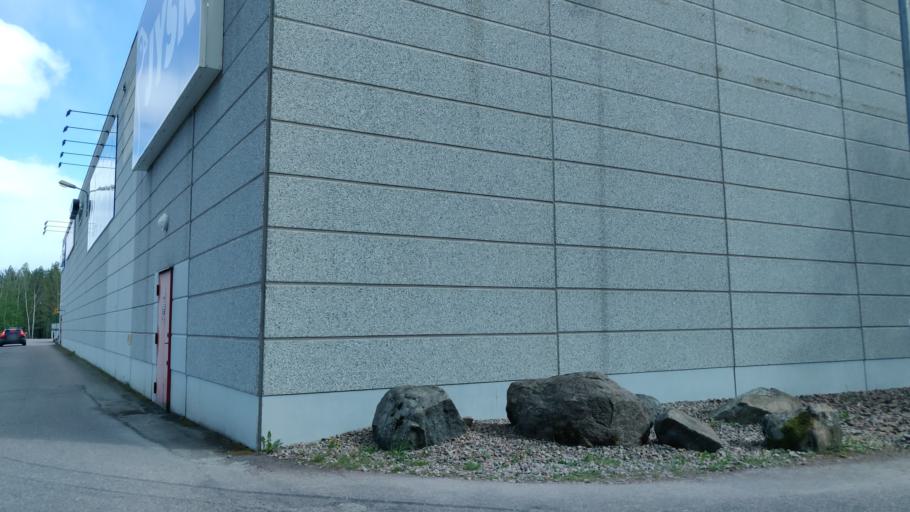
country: SE
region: Vaermland
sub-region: Hammaro Kommun
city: Skoghall
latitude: 59.3756
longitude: 13.4380
